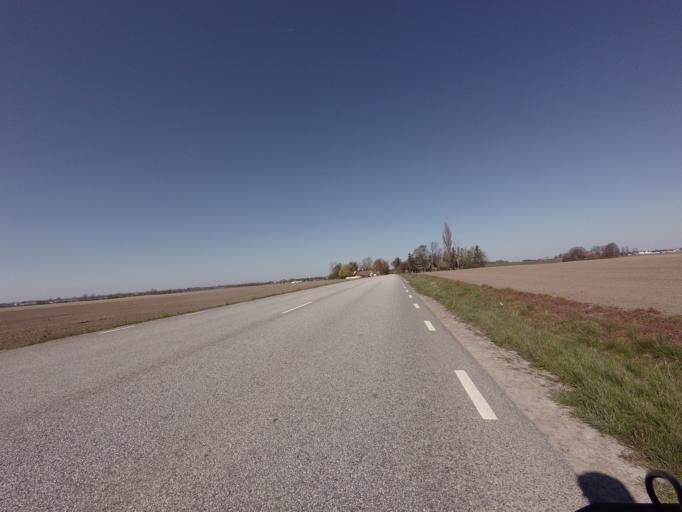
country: SE
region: Skane
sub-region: Vellinge Kommun
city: Vellinge
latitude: 55.4673
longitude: 13.0561
